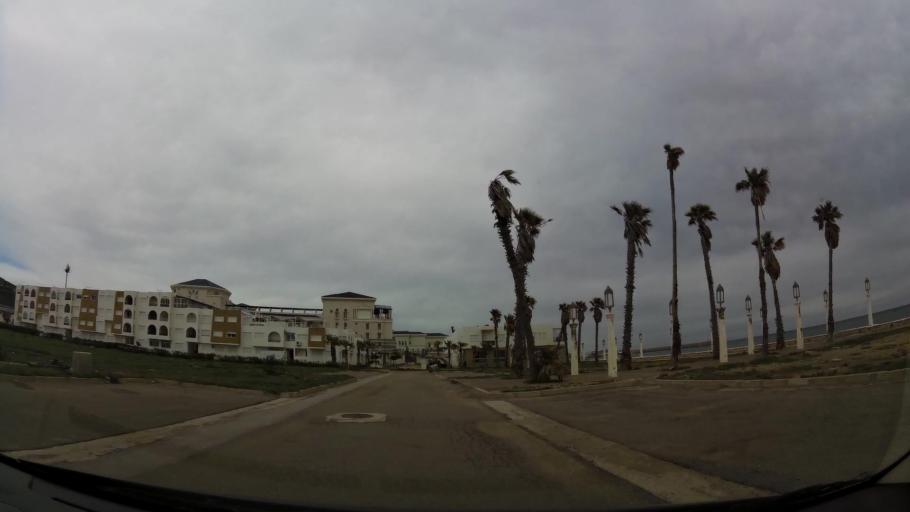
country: MA
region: Tanger-Tetouan
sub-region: Tetouan
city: Martil
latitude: 35.7446
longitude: -5.3423
